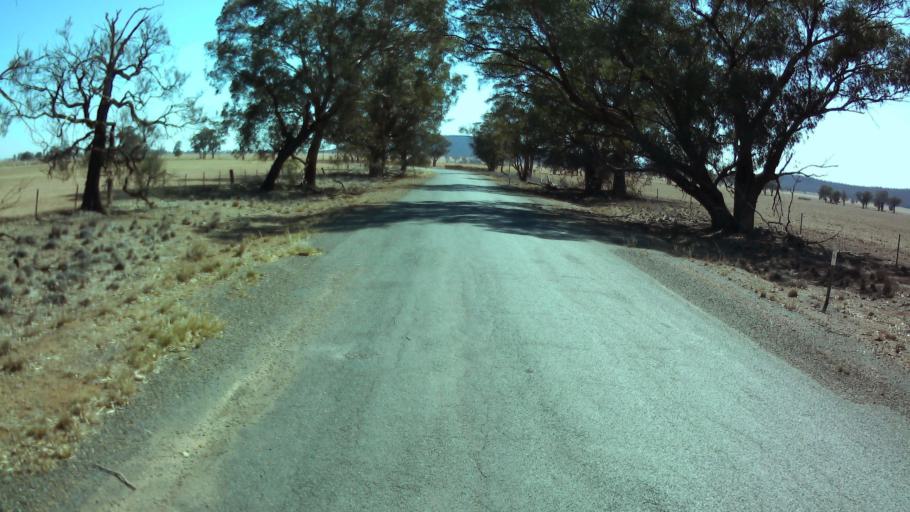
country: AU
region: New South Wales
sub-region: Weddin
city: Grenfell
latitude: -33.7067
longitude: 147.9164
